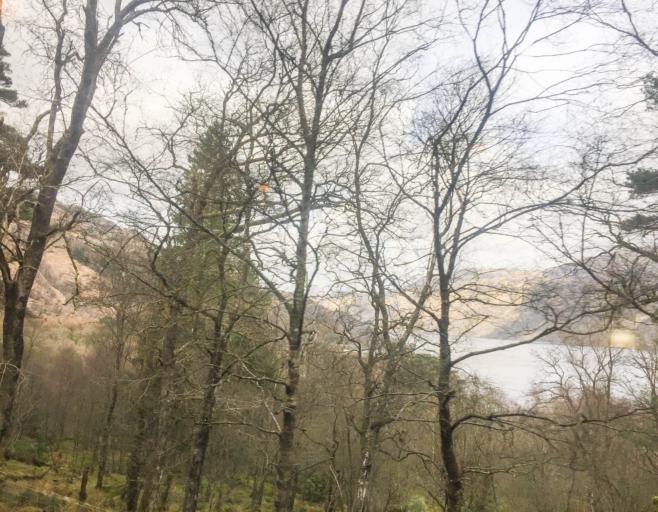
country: GB
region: Scotland
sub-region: Argyll and Bute
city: Garelochhead
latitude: 56.2415
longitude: -4.7128
